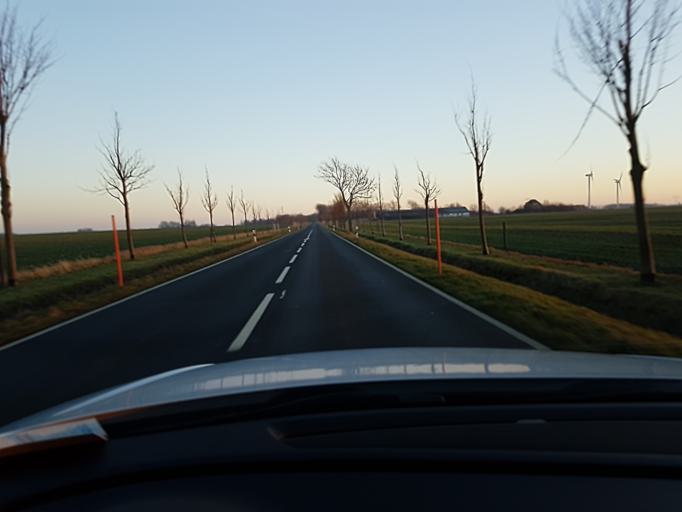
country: DE
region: Mecklenburg-Vorpommern
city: Wiek
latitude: 54.6071
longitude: 13.2827
